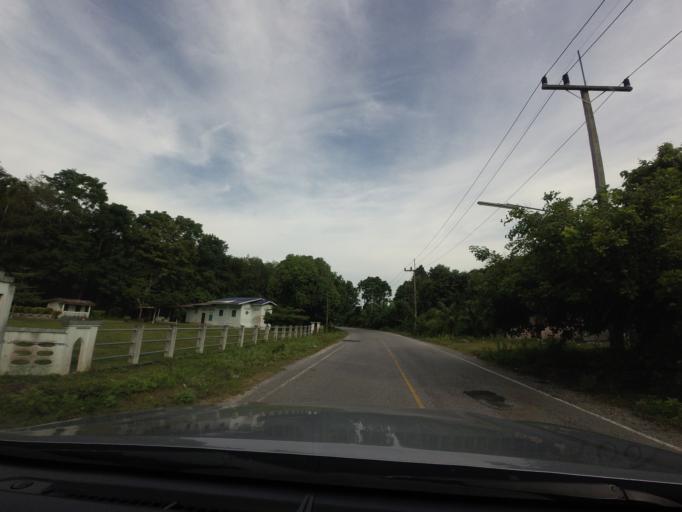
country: TH
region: Narathiwat
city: Rueso
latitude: 6.3453
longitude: 101.4799
